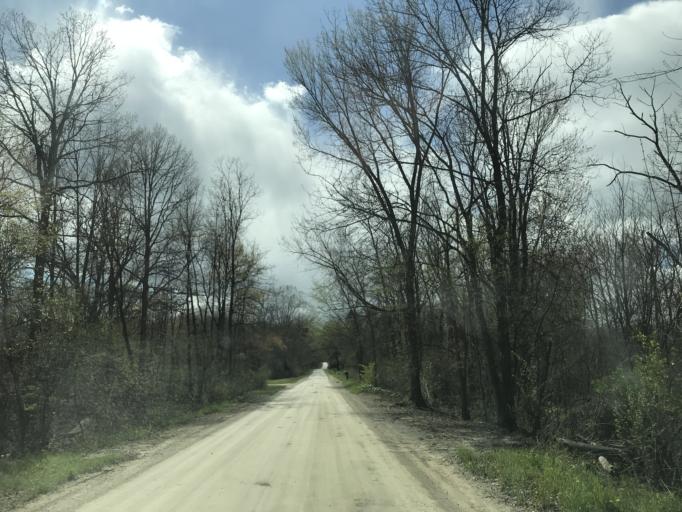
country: US
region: Michigan
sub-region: Livingston County
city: Whitmore Lake
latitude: 42.4029
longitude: -83.7128
